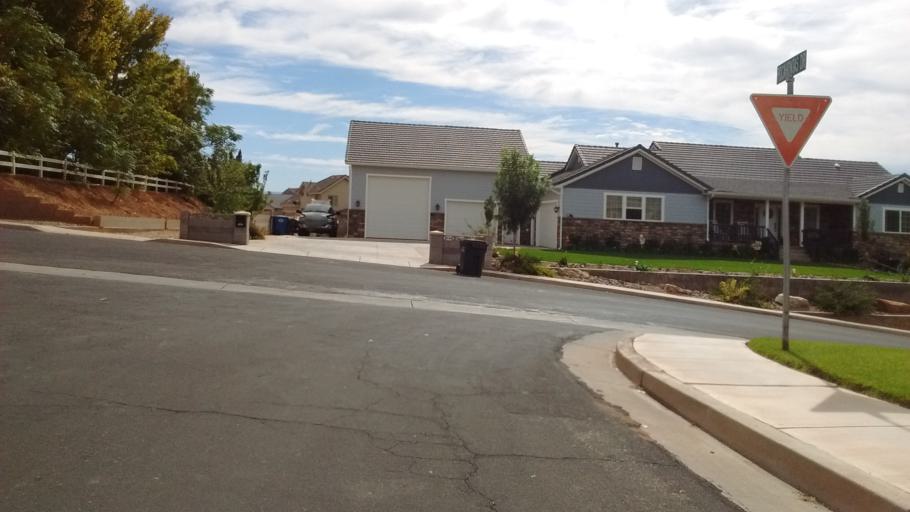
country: US
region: Utah
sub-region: Washington County
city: Washington
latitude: 37.1196
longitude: -113.4955
